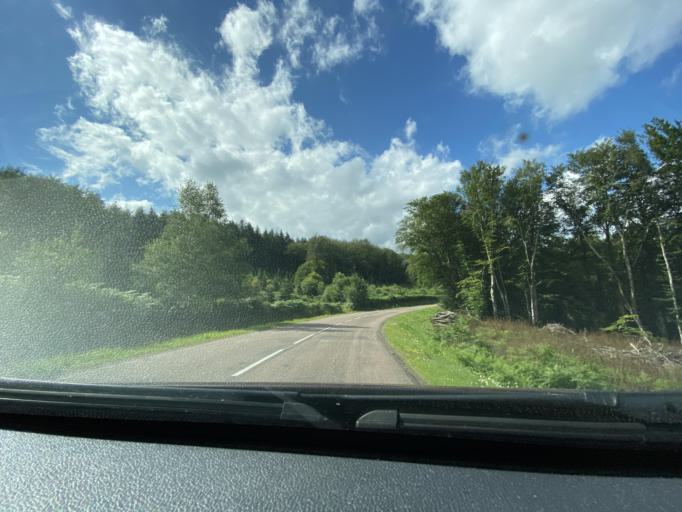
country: FR
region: Bourgogne
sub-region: Departement de la Cote-d'Or
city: Saulieu
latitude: 47.2636
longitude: 4.1244
